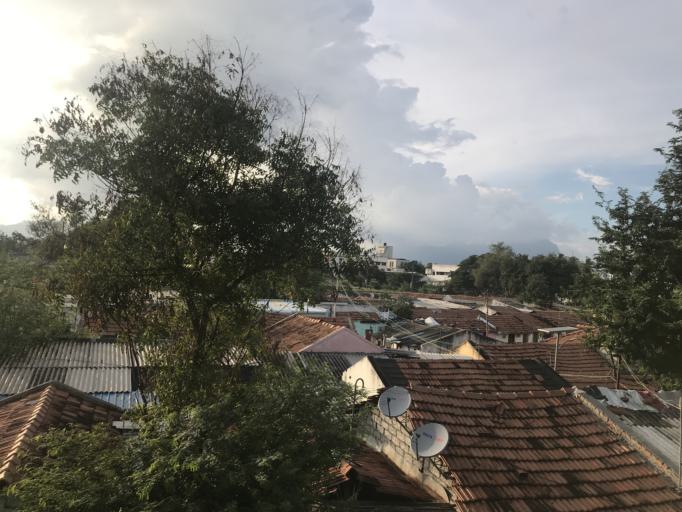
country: IN
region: Tamil Nadu
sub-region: Coimbatore
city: Coimbatore
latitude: 11.0275
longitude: 76.9539
